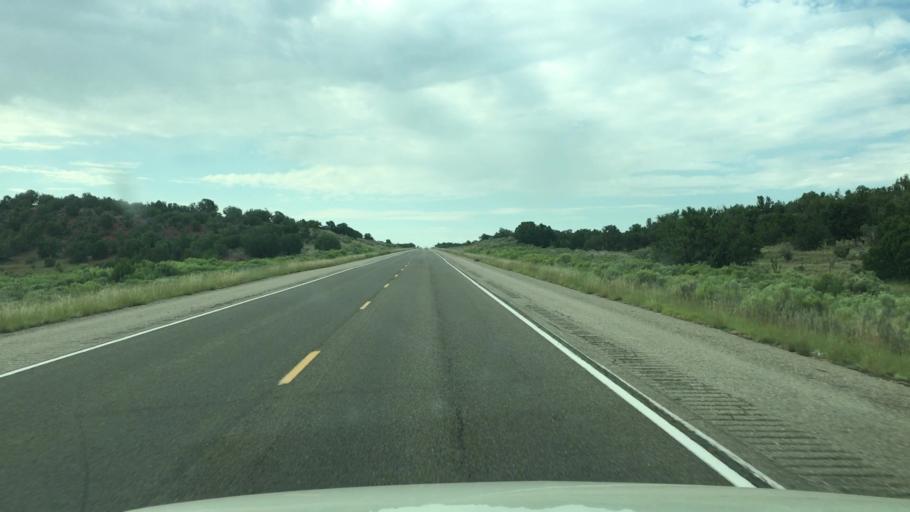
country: US
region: New Mexico
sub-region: Santa Fe County
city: Eldorado at Santa Fe
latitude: 35.2359
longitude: -105.8043
